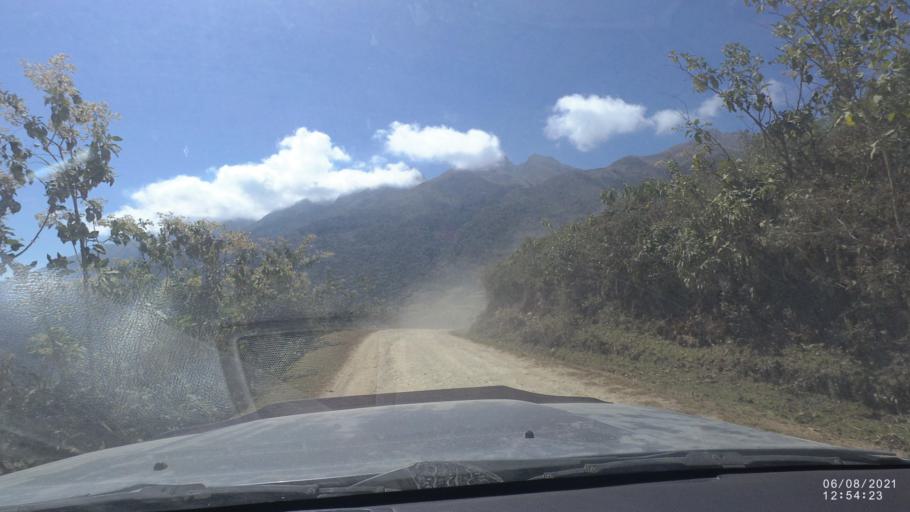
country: BO
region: Cochabamba
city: Colchani
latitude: -16.7582
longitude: -66.6834
